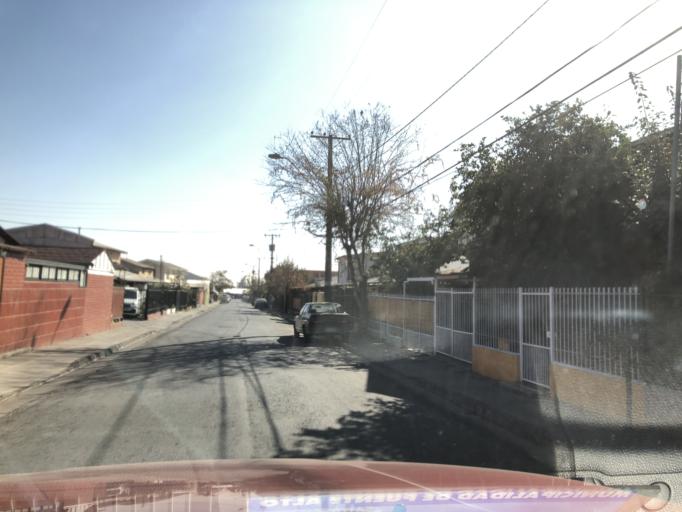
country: CL
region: Santiago Metropolitan
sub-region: Provincia de Cordillera
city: Puente Alto
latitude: -33.5753
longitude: -70.5736
